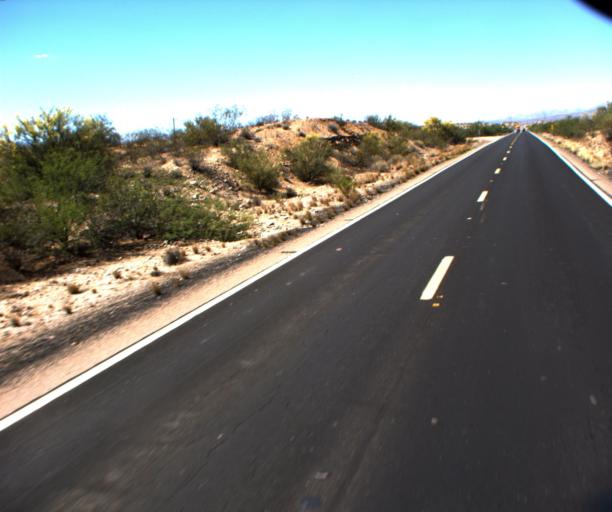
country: US
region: Arizona
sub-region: Yavapai County
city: Bagdad
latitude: 34.7316
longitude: -113.6152
